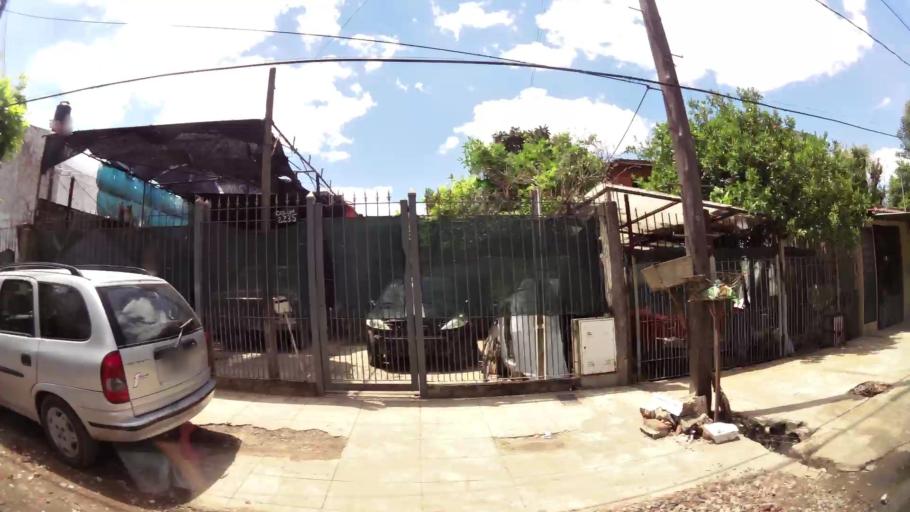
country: AR
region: Buenos Aires
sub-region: Partido de Lanus
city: Lanus
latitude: -34.7194
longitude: -58.4188
